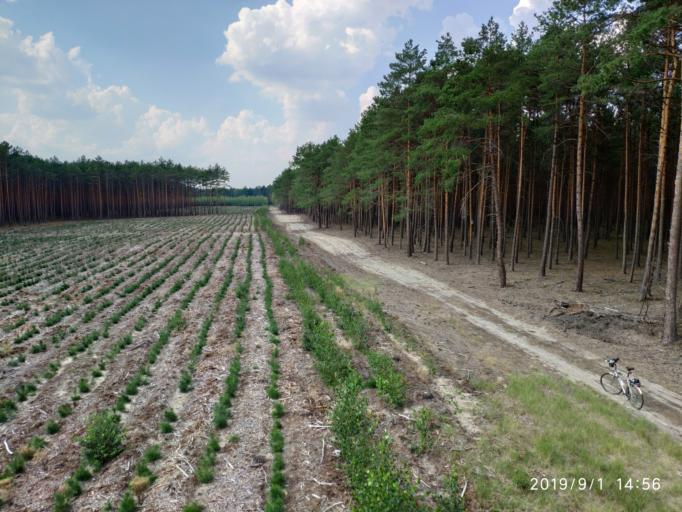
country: PL
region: Lubusz
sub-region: Powiat zielonogorski
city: Babimost
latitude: 52.1112
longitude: 15.8104
